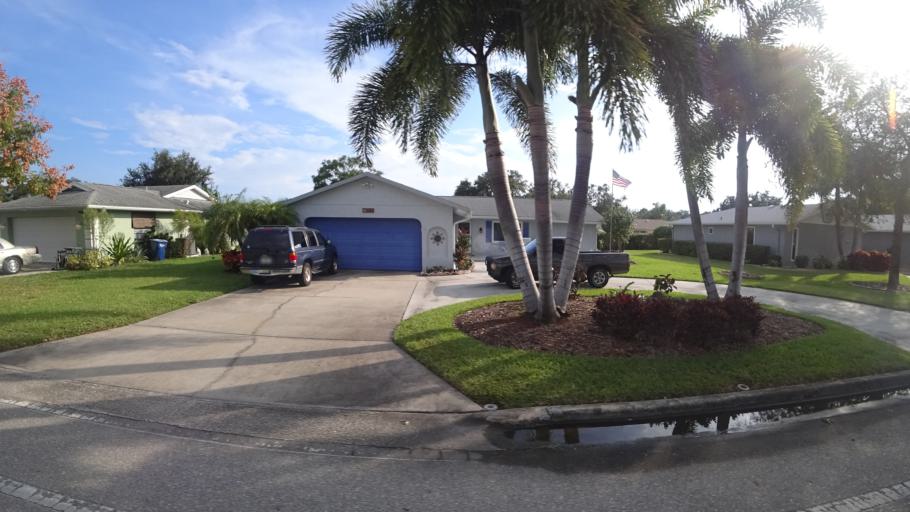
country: US
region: Florida
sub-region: Manatee County
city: West Bradenton
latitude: 27.4848
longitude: -82.6152
